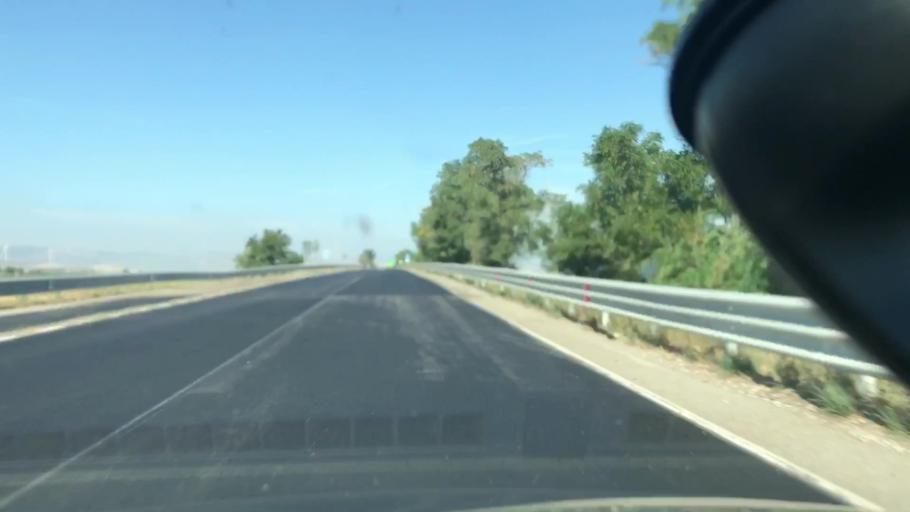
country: IT
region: Basilicate
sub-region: Provincia di Potenza
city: Zona 179
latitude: 41.0749
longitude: 15.6439
